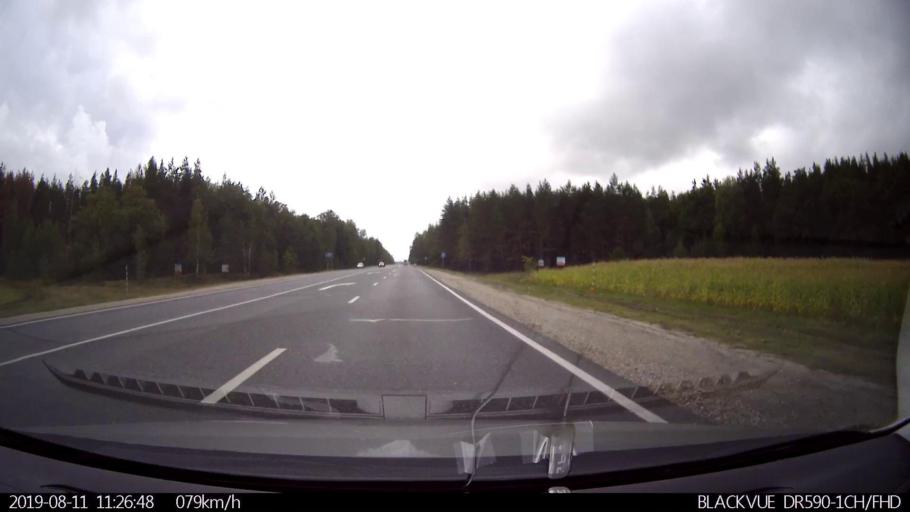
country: RU
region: Ulyanovsk
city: Krasnyy Gulyay
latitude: 54.1008
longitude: 48.2338
